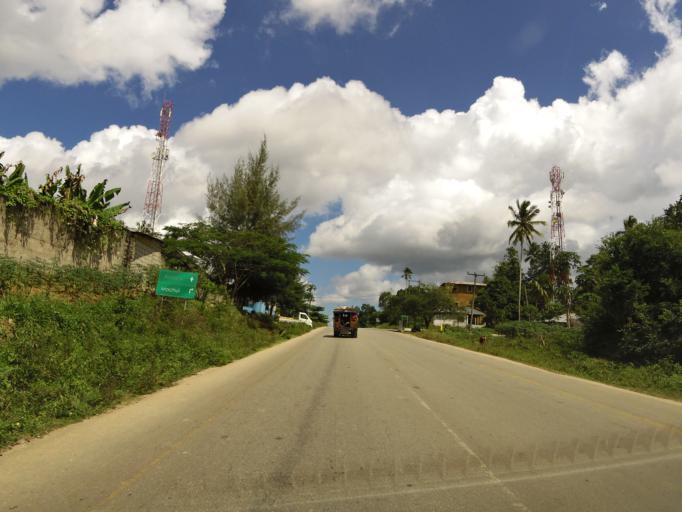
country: TZ
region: Zanzibar Central/South
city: Koani
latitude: -6.1363
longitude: 39.2888
